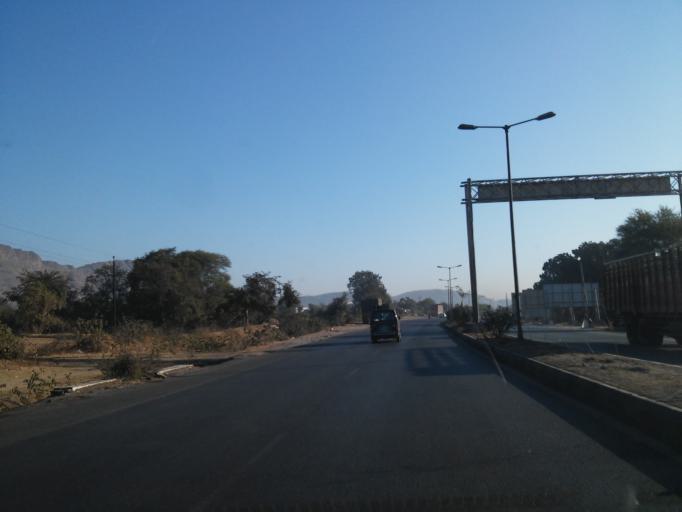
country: IN
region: Rajasthan
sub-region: Dungarpur
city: Dungarpur
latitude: 23.9949
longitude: 73.6298
